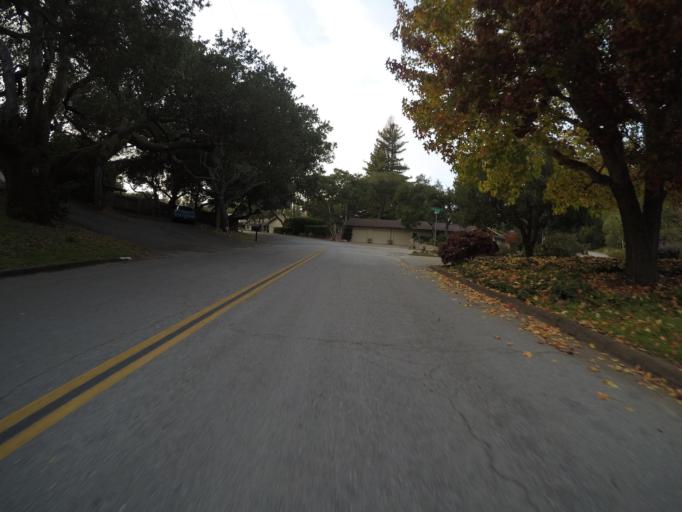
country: US
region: California
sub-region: Santa Cruz County
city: Pasatiempo
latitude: 37.0230
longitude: -122.0349
